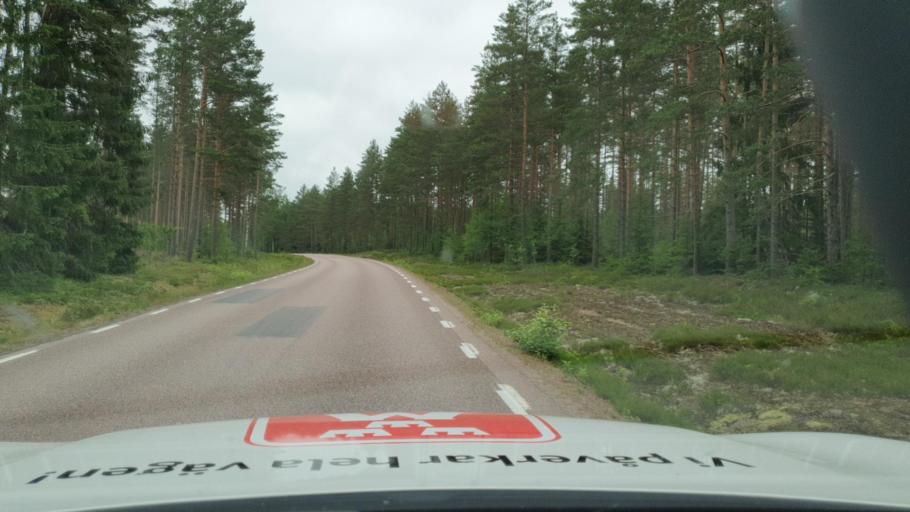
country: SE
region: Vaermland
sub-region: Kristinehamns Kommun
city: Kristinehamn
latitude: 59.5085
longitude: 13.9538
